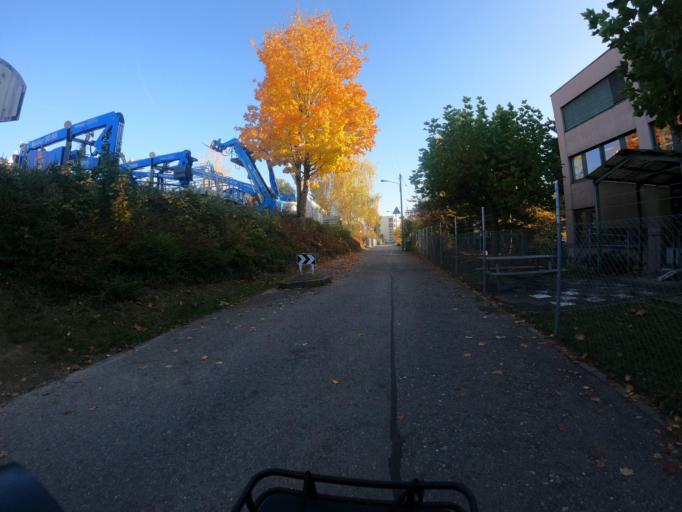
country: CH
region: Zurich
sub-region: Bezirk Affoltern
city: Affoltern / Oberdorf
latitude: 47.2757
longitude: 8.4407
